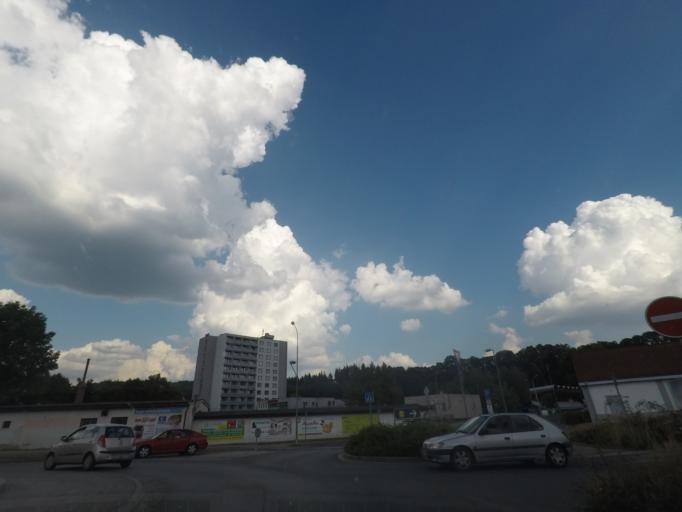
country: CZ
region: Kralovehradecky
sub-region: Okres Trutnov
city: Trutnov
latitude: 50.5652
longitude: 15.9236
